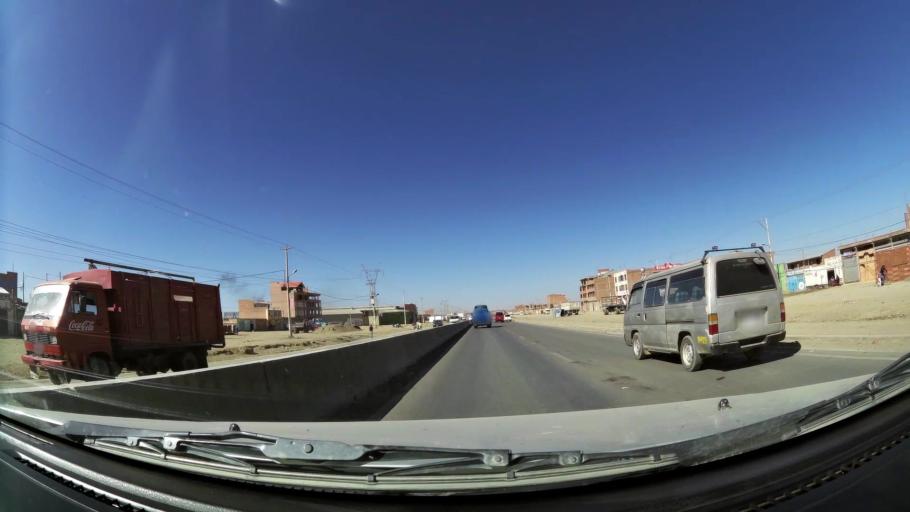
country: BO
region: La Paz
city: La Paz
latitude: -16.6028
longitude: -68.1830
